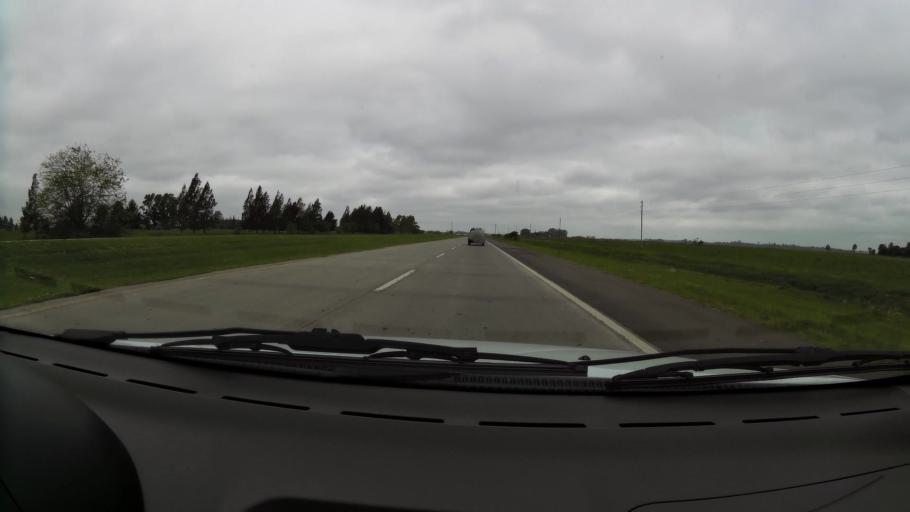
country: AR
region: Buenos Aires
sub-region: Partido de Brandsen
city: Brandsen
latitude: -35.0389
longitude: -58.1835
